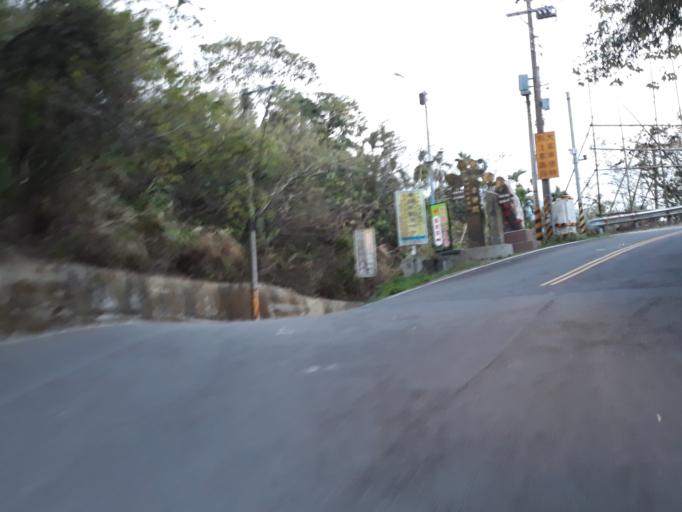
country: TW
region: Taiwan
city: Fengyuan
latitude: 24.3604
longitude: 120.8692
